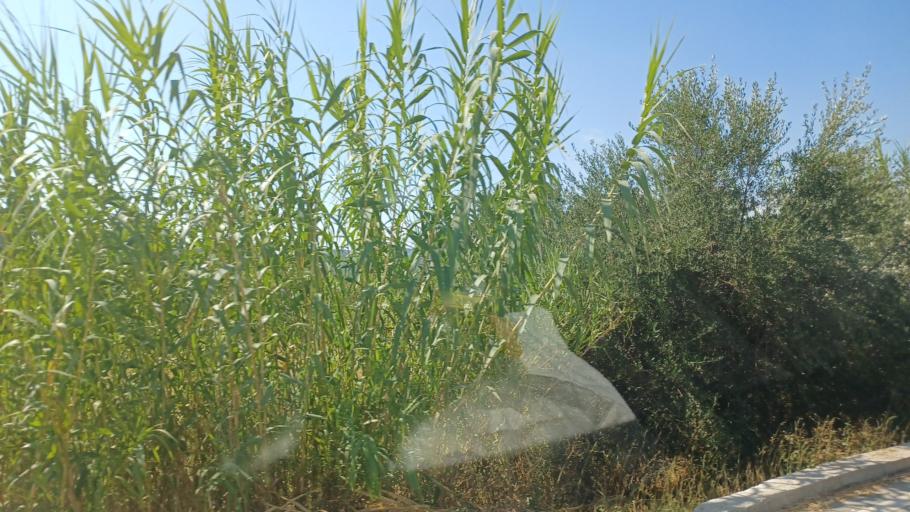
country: CY
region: Pafos
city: Tala
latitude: 34.8890
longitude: 32.4856
